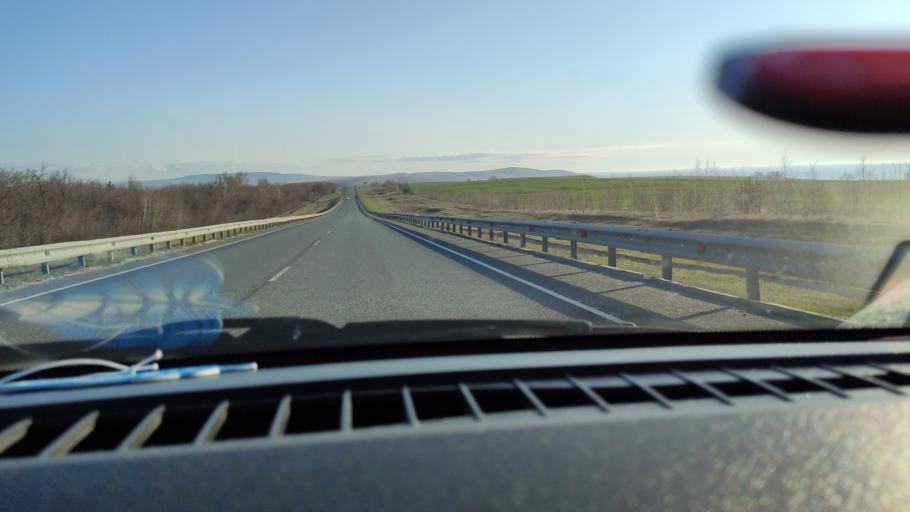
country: RU
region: Saratov
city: Balakovo
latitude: 52.1723
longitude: 47.8321
